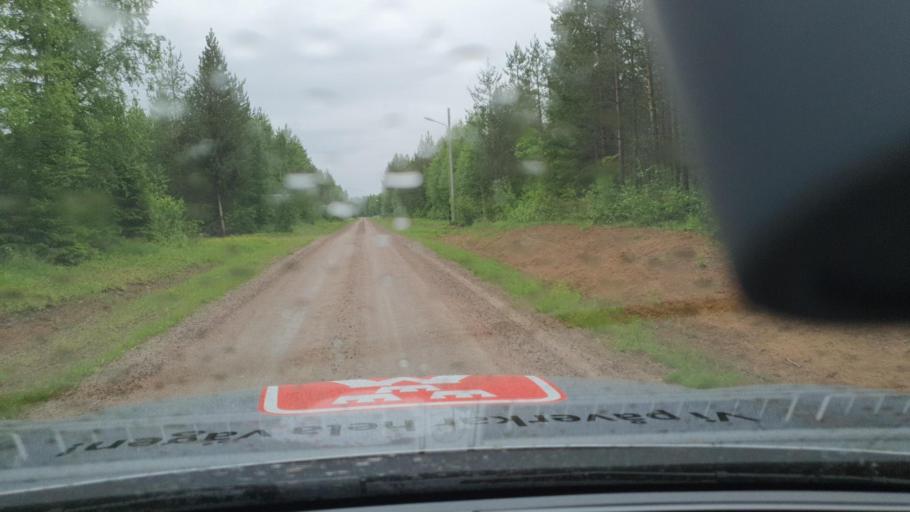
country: SE
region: Norrbotten
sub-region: Overkalix Kommun
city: OEverkalix
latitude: 66.5469
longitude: 22.7447
